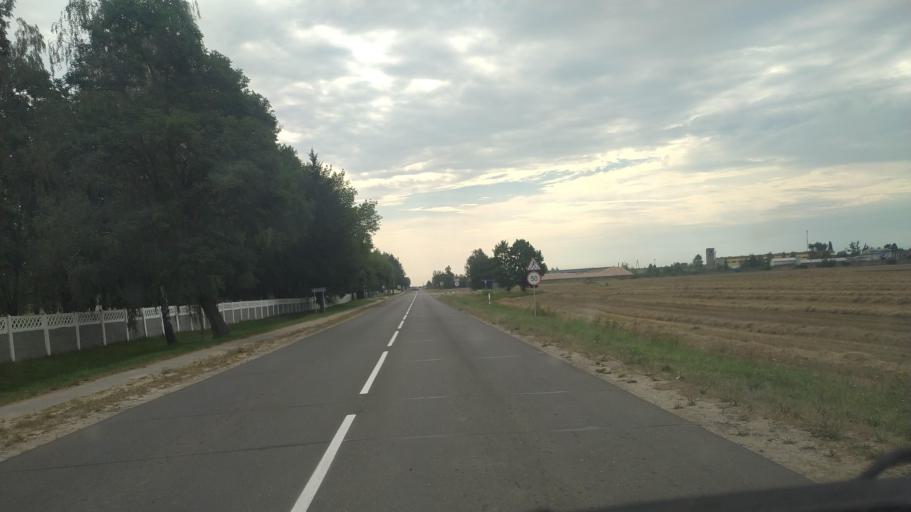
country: BY
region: Brest
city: Byaroza
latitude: 52.5549
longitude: 24.9230
